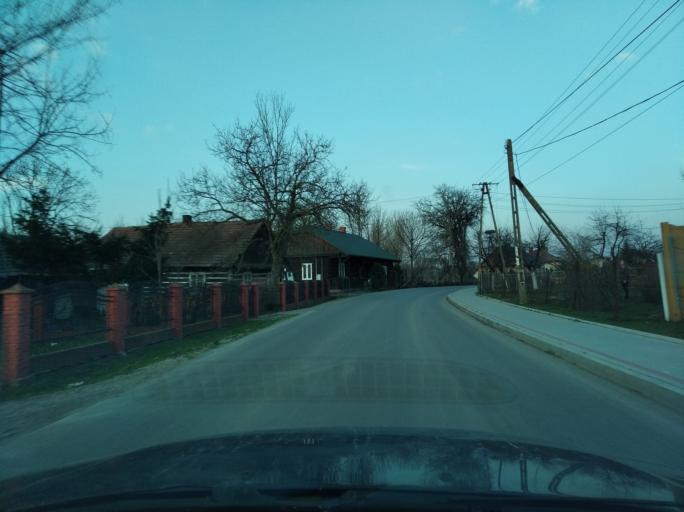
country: PL
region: Subcarpathian Voivodeship
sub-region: Powiat przeworski
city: Zurawiczki
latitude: 50.0112
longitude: 22.4933
